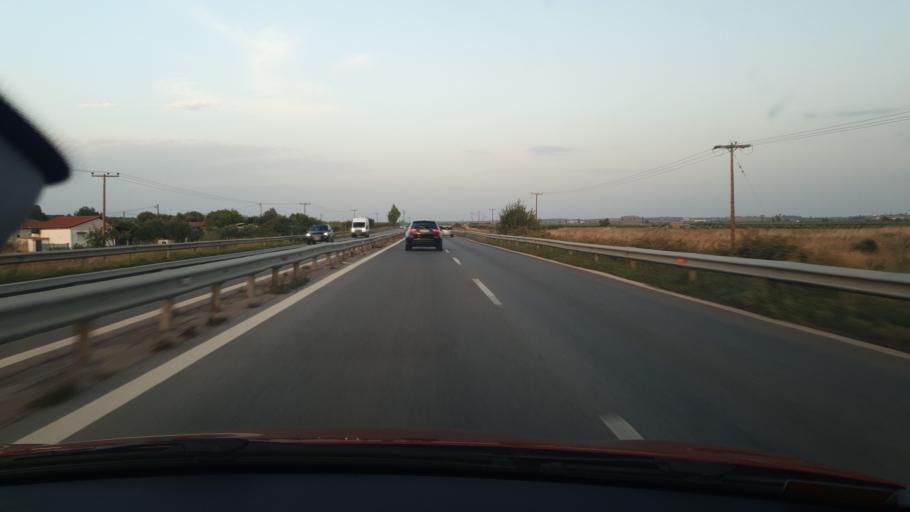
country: GR
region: Central Macedonia
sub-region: Nomos Chalkidikis
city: Nea Plagia
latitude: 40.2844
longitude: 23.1762
